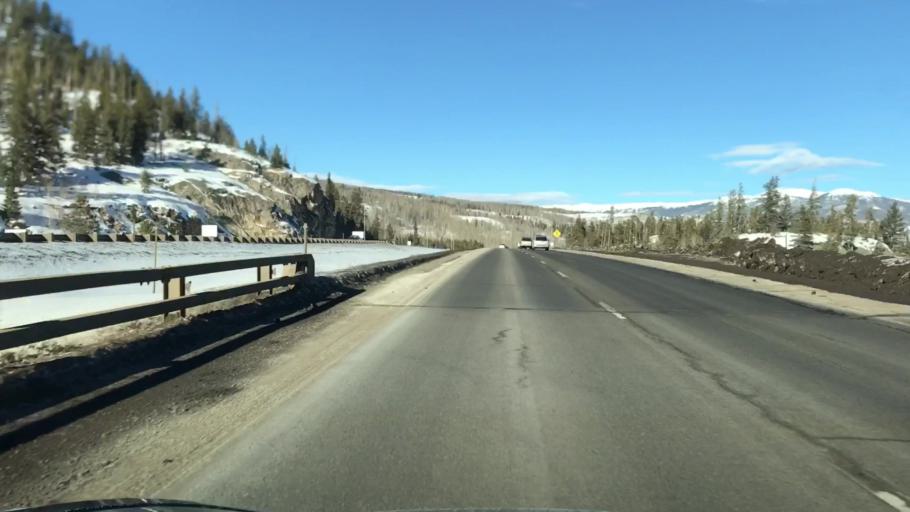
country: US
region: Colorado
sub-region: Summit County
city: Frisco
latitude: 39.5758
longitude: -106.1125
